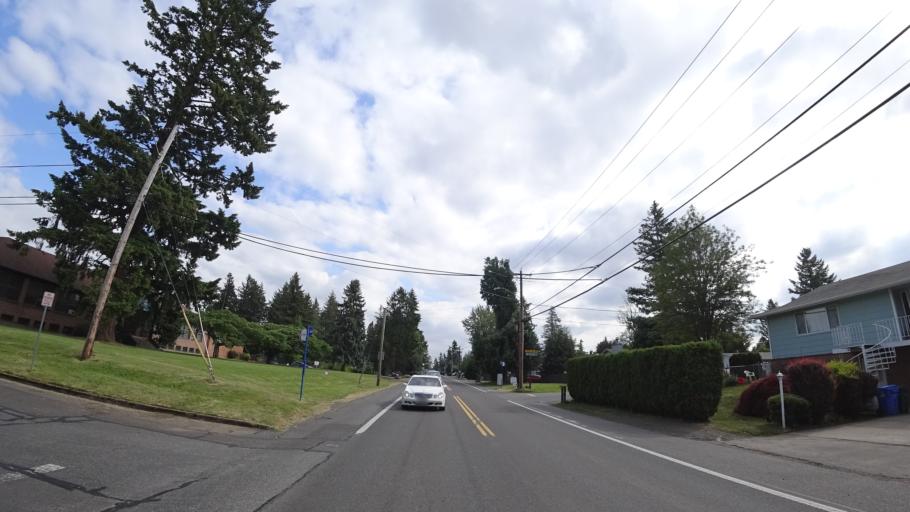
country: US
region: Oregon
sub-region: Multnomah County
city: Fairview
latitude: 45.5301
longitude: -122.4961
